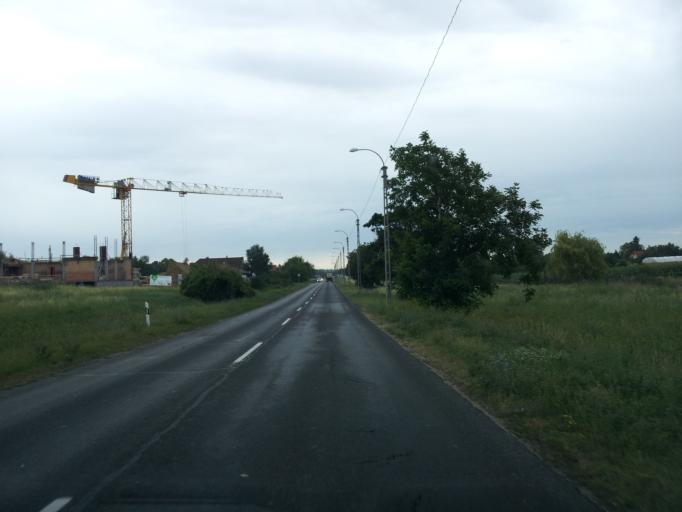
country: HU
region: Fejer
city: Kapolnasnyek
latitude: 47.2412
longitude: 18.6684
